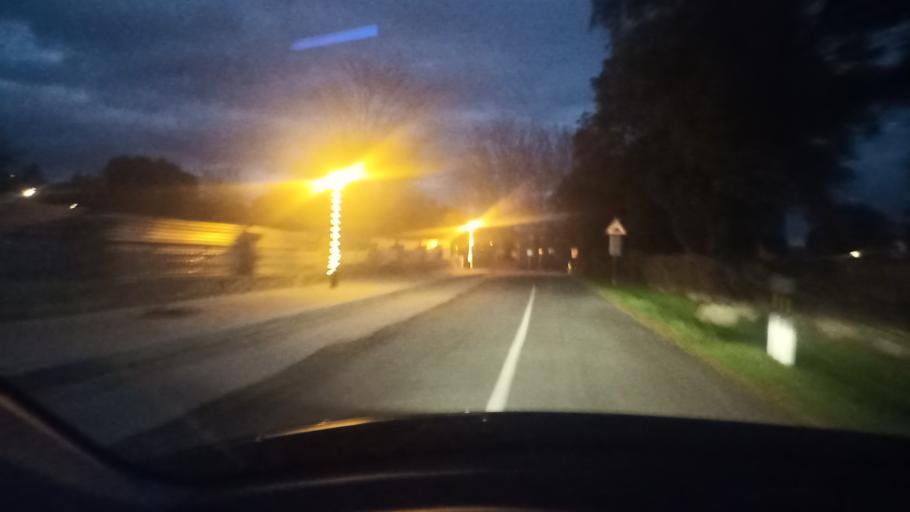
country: ES
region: Madrid
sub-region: Provincia de Madrid
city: Colmenar del Arroyo
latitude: 40.4232
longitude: -4.2007
